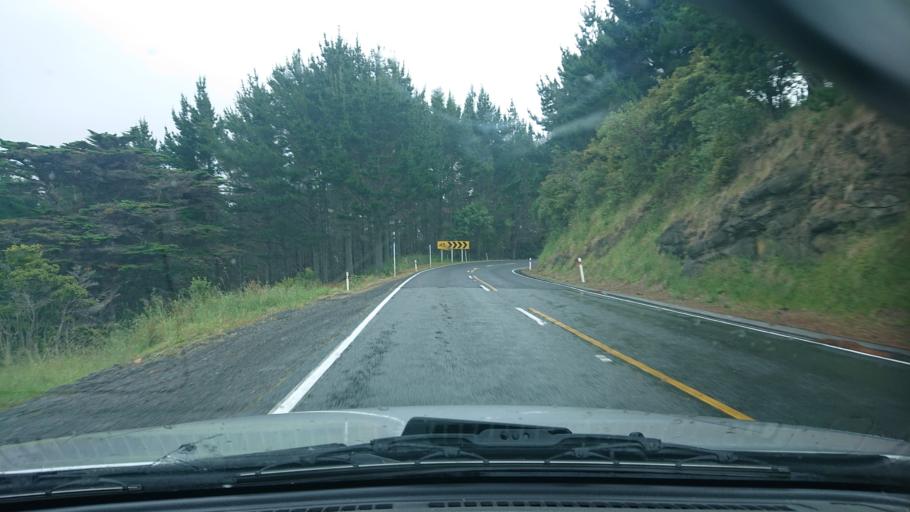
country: NZ
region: Auckland
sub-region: Auckland
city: Wellsford
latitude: -36.3594
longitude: 174.4676
